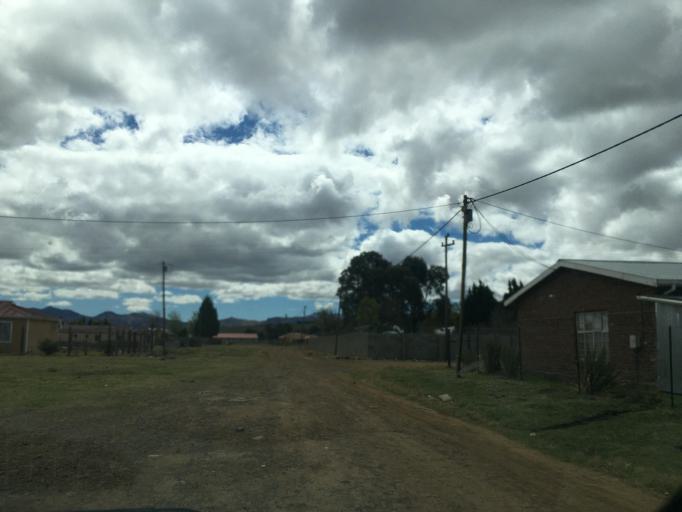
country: ZA
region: Eastern Cape
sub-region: Chris Hani District Municipality
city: Elliot
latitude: -31.3325
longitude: 27.8450
